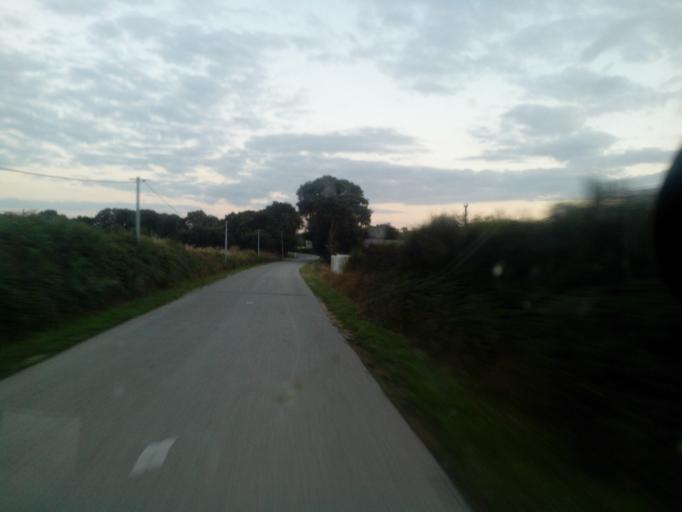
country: FR
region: Brittany
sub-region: Departement du Morbihan
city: Plumelec
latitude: 47.8475
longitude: -2.6360
